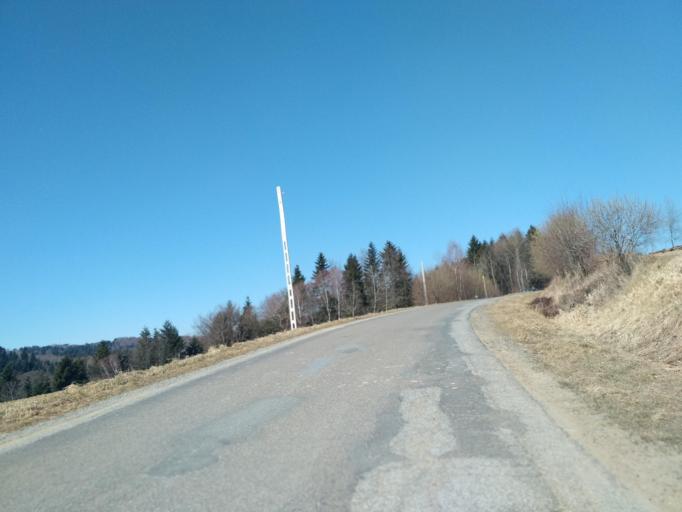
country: PL
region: Subcarpathian Voivodeship
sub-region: Powiat debicki
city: Brzostek
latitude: 49.9474
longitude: 21.4302
